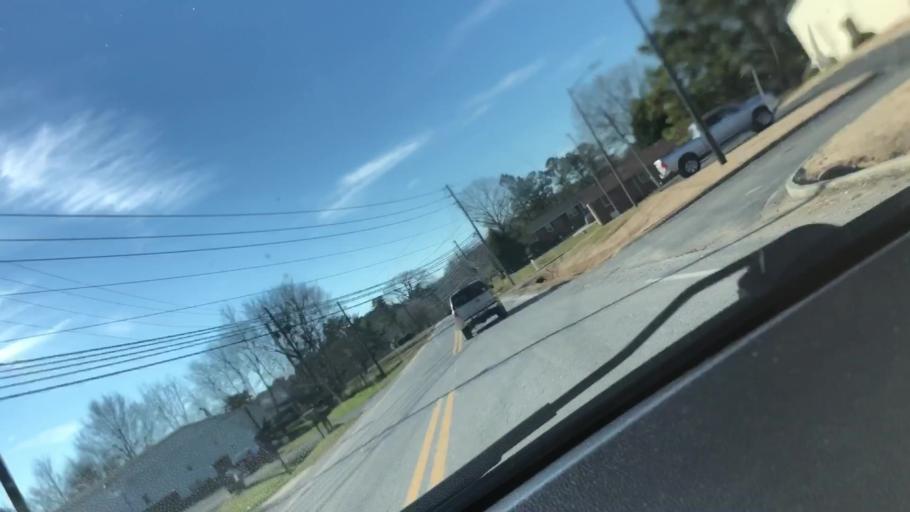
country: US
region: Georgia
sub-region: Bartow County
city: Cartersville
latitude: 34.2229
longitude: -84.8153
